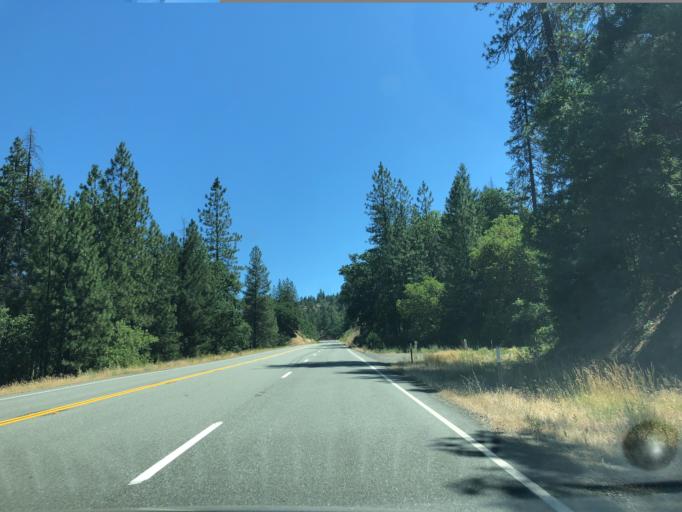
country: US
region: California
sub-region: Trinity County
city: Weaverville
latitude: 40.6667
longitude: -122.8905
